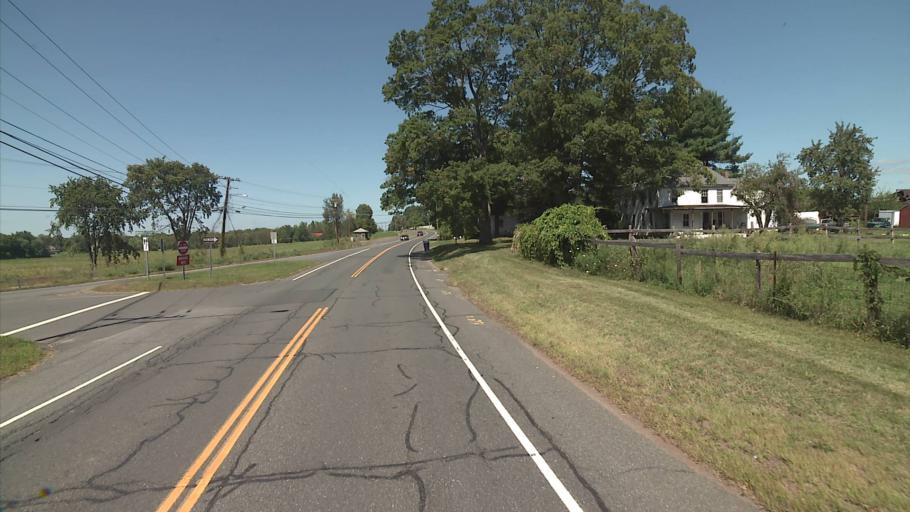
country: US
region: Connecticut
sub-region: Hartford County
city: Thompsonville
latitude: 42.0196
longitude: -72.6169
